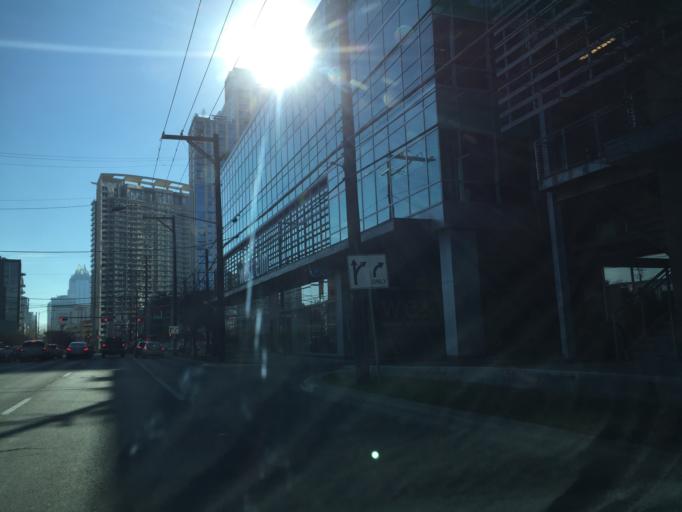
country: US
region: Texas
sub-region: Travis County
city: Austin
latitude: 30.2706
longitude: -97.7556
